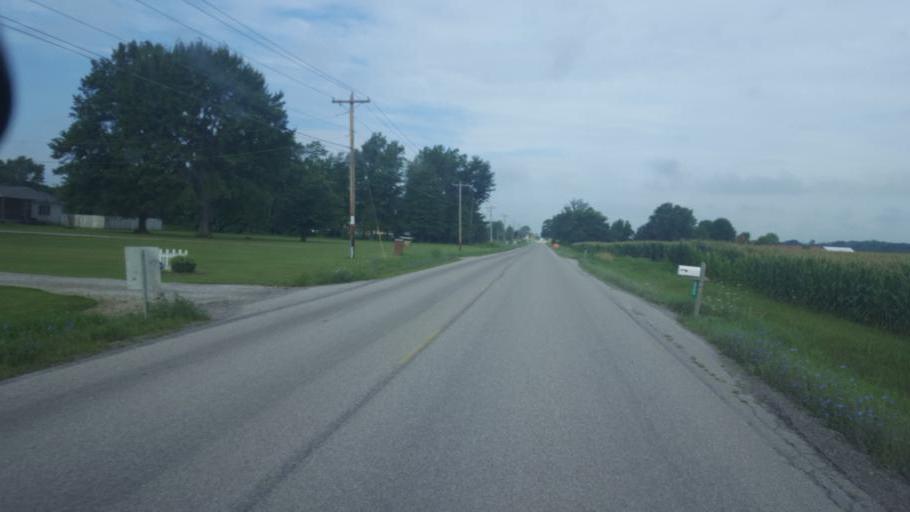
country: US
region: Ohio
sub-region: Delaware County
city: Ashley
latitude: 40.4065
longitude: -82.8856
